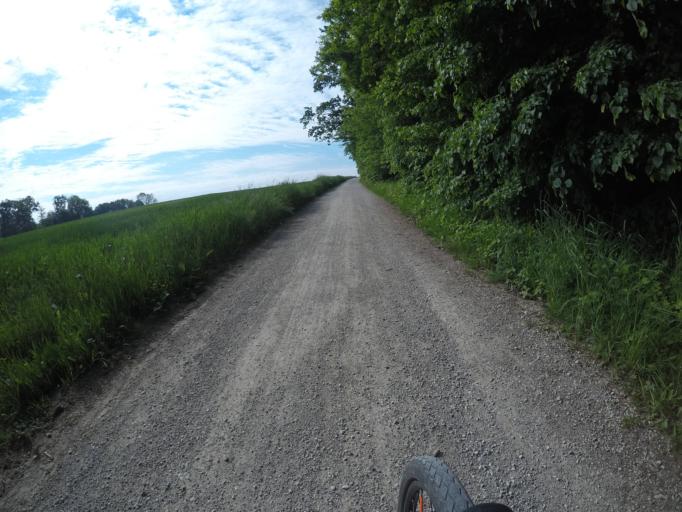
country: DE
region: Baden-Wuerttemberg
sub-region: Regierungsbezirk Stuttgart
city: Denkendorf
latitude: 48.6664
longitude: 9.3204
